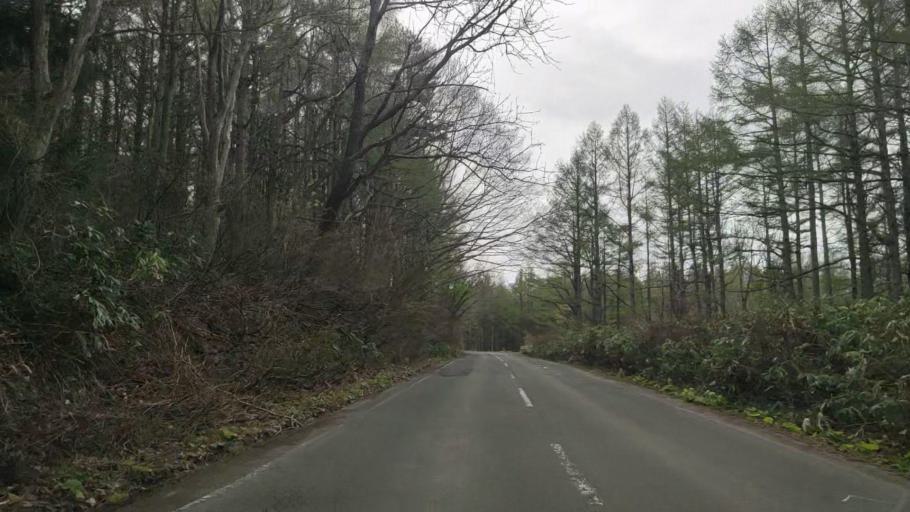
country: JP
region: Aomori
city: Aomori Shi
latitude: 40.7298
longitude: 140.8455
